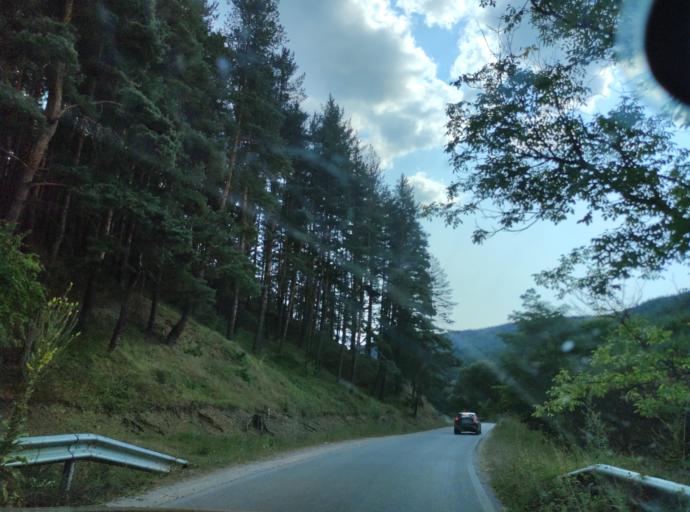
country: BG
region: Blagoevgrad
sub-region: Obshtina Belitsa
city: Belitsa
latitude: 41.9681
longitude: 23.5565
